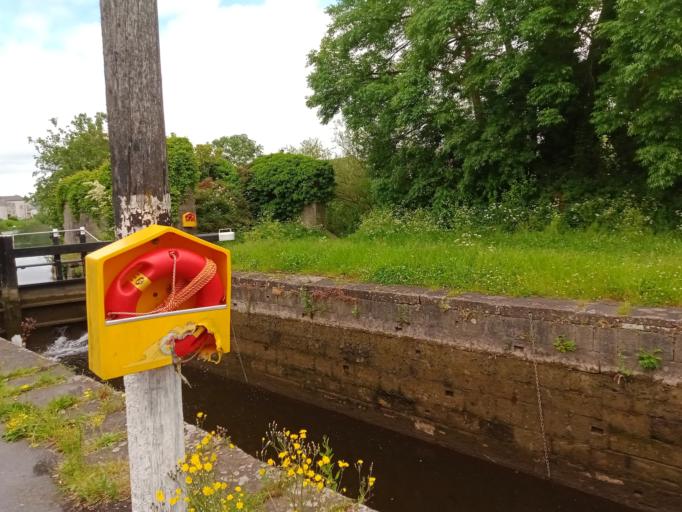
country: IE
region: Leinster
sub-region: County Carlow
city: Carlow
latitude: 52.8343
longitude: -6.9381
